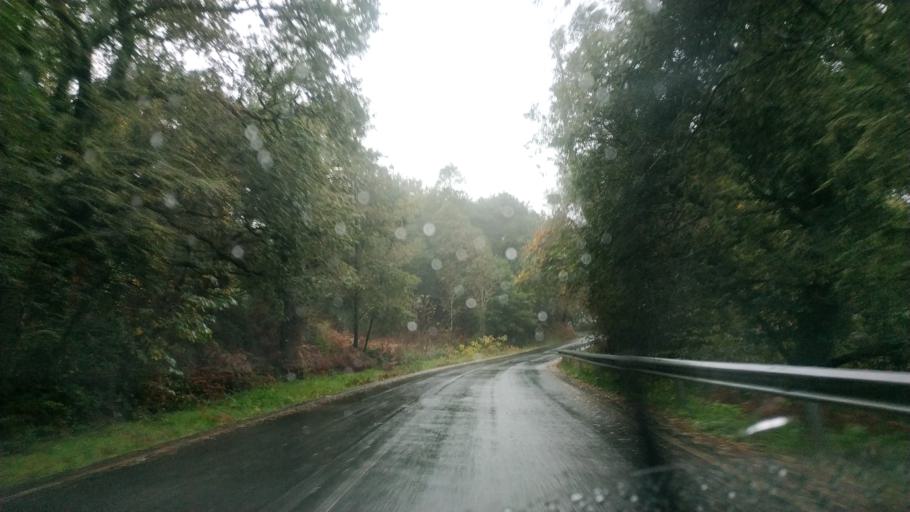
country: ES
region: Galicia
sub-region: Provincia da Coruna
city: Negreira
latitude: 42.9076
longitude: -8.7474
